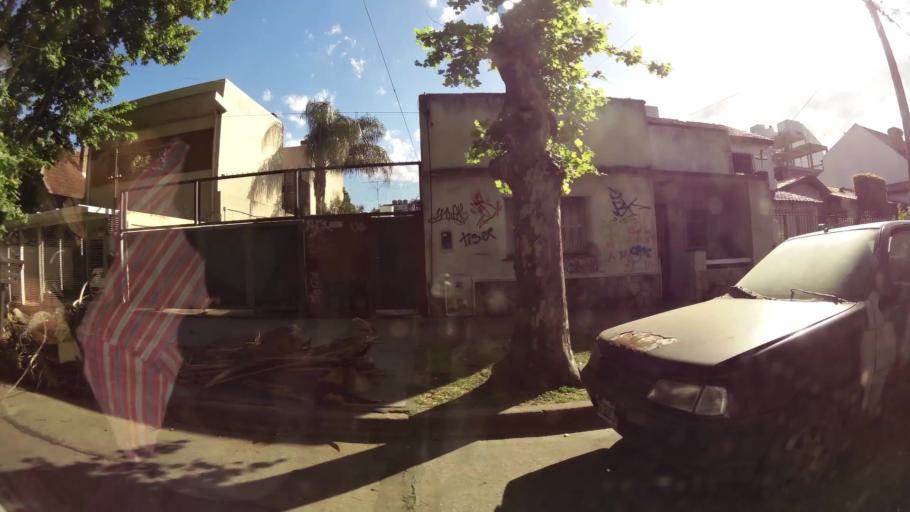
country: AR
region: Buenos Aires
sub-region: Partido de General San Martin
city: General San Martin
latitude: -34.5465
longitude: -58.5490
